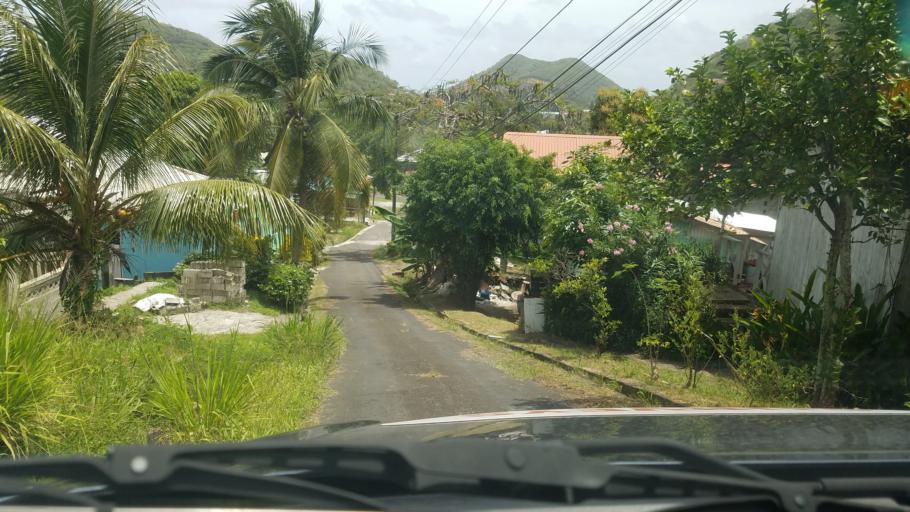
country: LC
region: Castries Quarter
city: Bisee
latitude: 14.0442
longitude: -60.9648
